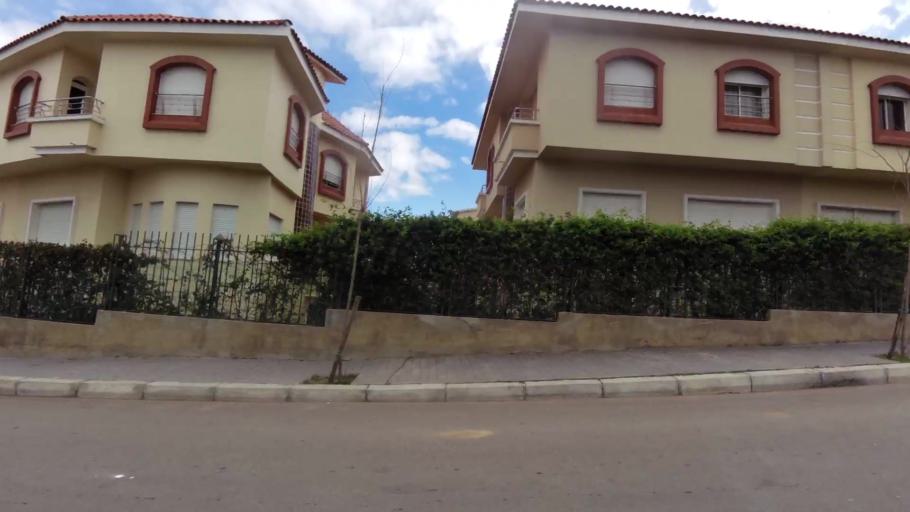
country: MA
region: Tanger-Tetouan
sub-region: Tanger-Assilah
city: Boukhalef
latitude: 35.7705
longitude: -5.8622
